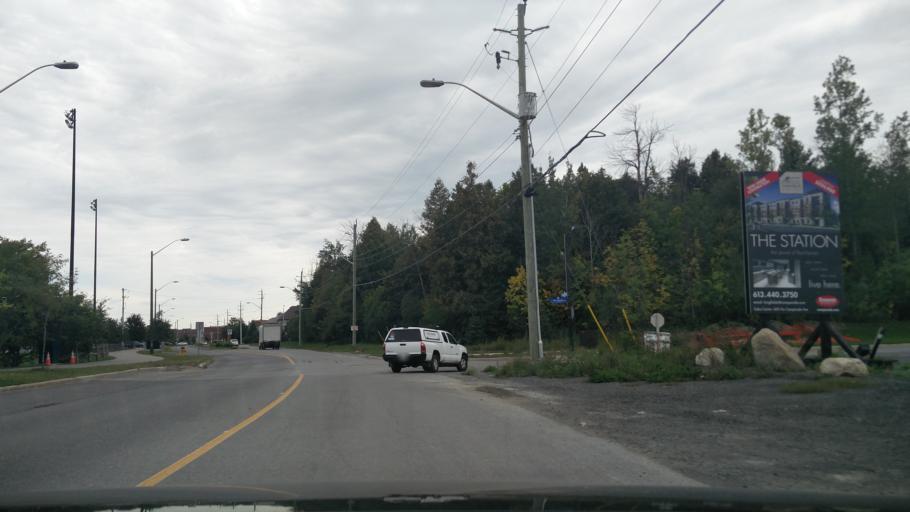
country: CA
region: Ontario
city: Bells Corners
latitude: 45.2823
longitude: -75.7448
